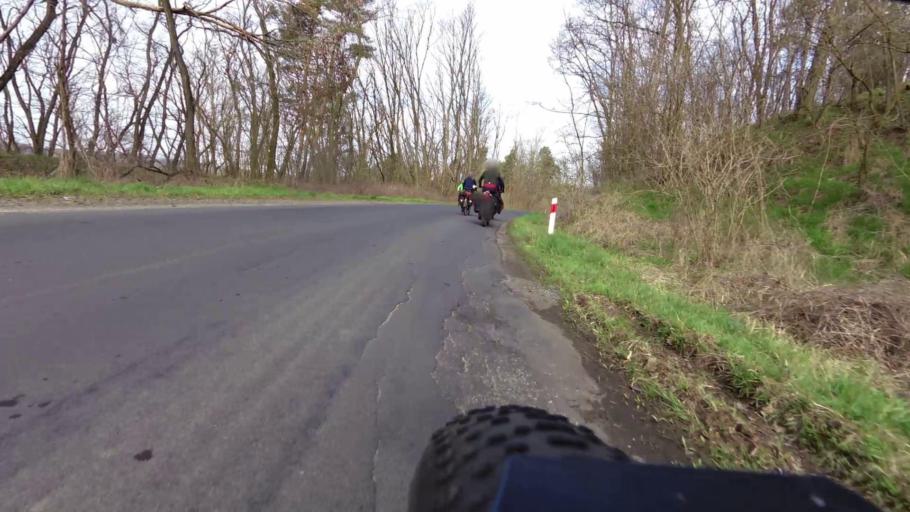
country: DE
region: Brandenburg
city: Brieskow-Finkenheerd
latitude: 52.2946
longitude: 14.6043
